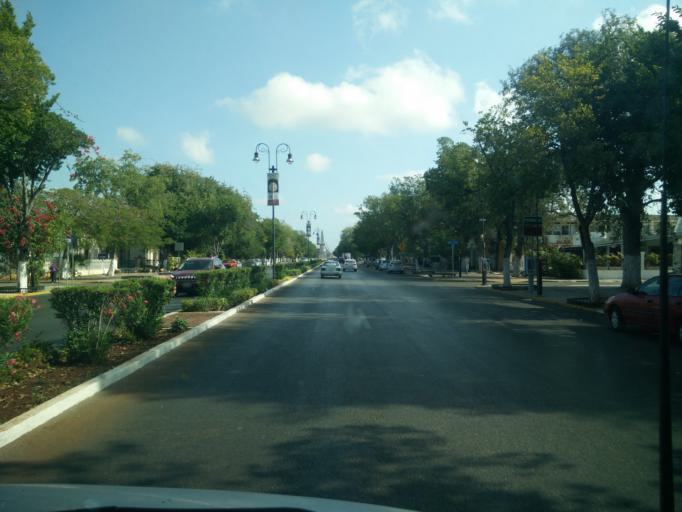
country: MX
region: Yucatan
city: Merida
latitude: 20.9798
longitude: -89.6186
